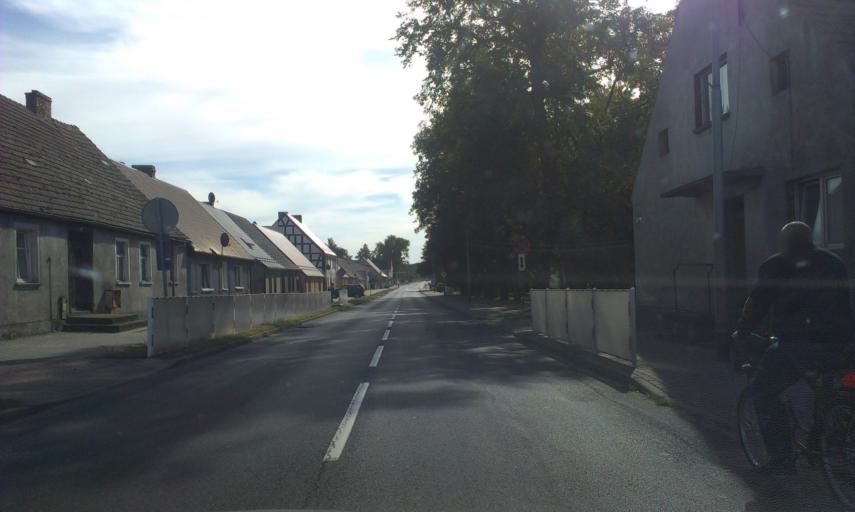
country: PL
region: Greater Poland Voivodeship
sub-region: Powiat zlotowski
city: Okonek
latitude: 53.5383
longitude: 16.8496
